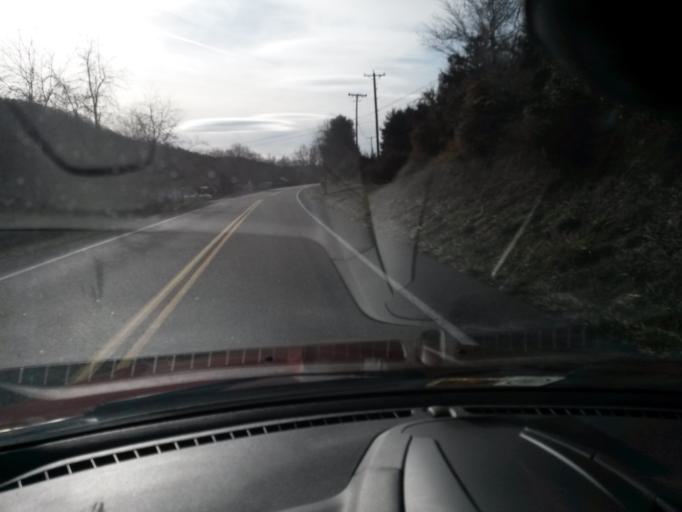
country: US
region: Virginia
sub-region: Augusta County
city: Jolivue
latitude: 38.0998
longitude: -79.3249
